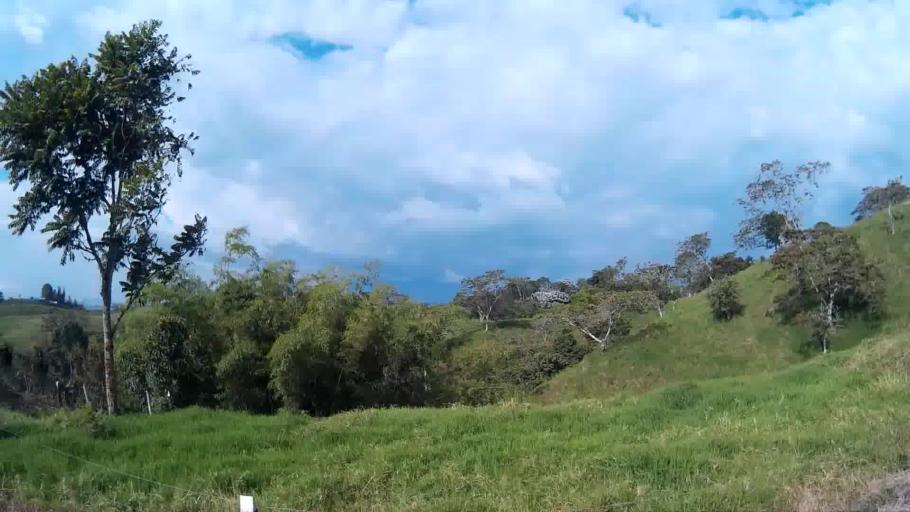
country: CO
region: Quindio
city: Filandia
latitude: 4.7001
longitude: -75.6798
